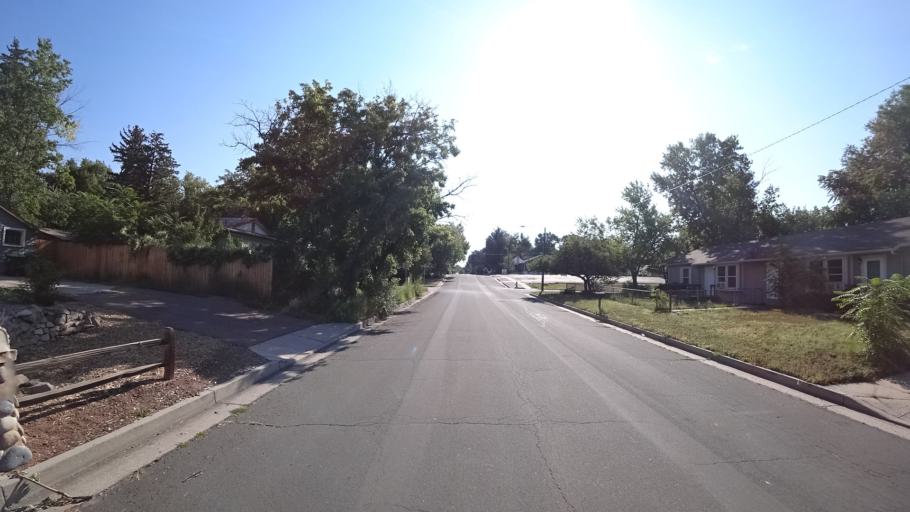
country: US
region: Colorado
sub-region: El Paso County
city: Colorado Springs
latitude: 38.8724
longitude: -104.8288
